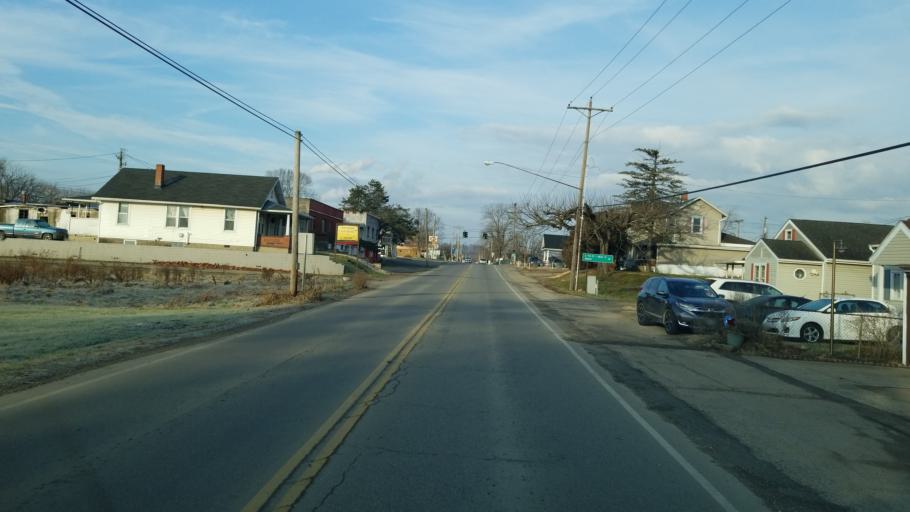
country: US
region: Ohio
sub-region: Ross County
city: Chillicothe
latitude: 39.3240
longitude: -82.9586
